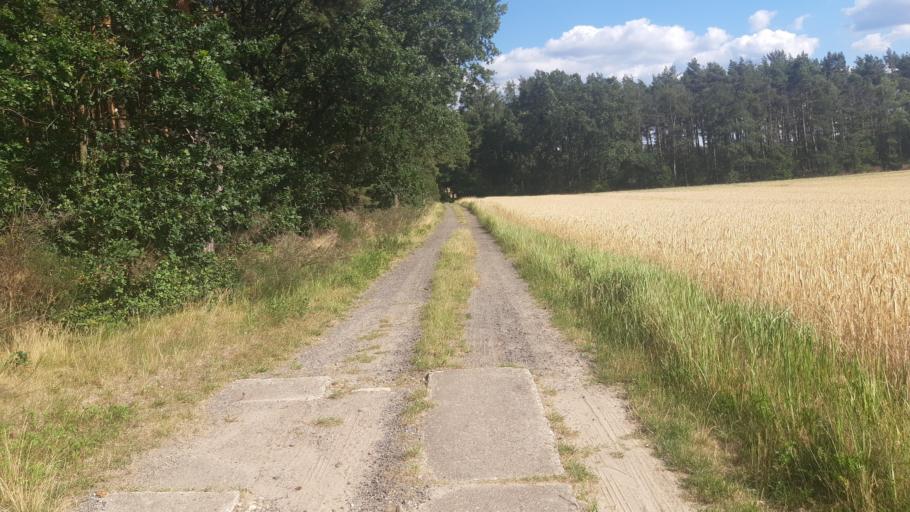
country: DE
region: Lower Saxony
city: Dahlem
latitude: 53.1990
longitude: 10.7649
